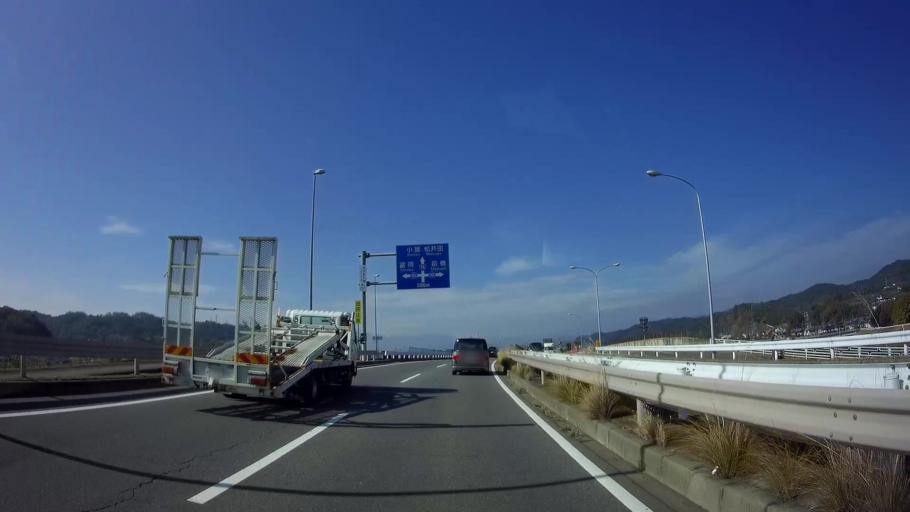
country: JP
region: Gunma
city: Annaka
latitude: 36.3335
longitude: 138.9337
